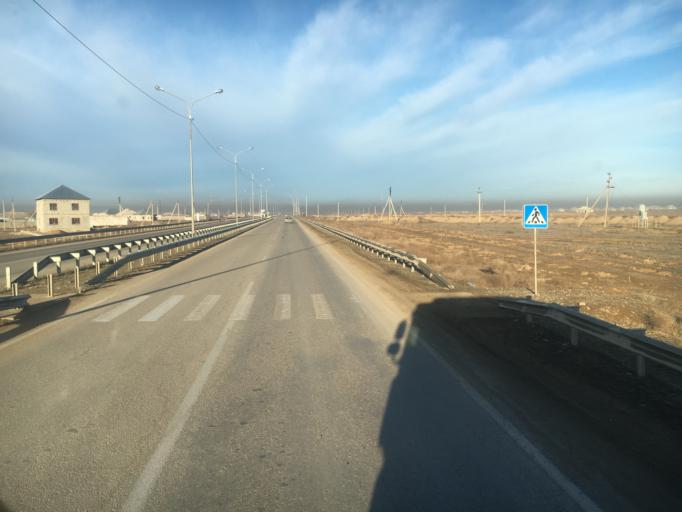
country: KZ
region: Ongtustik Qazaqstan
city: Turkestan
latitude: 43.3029
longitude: 68.3316
